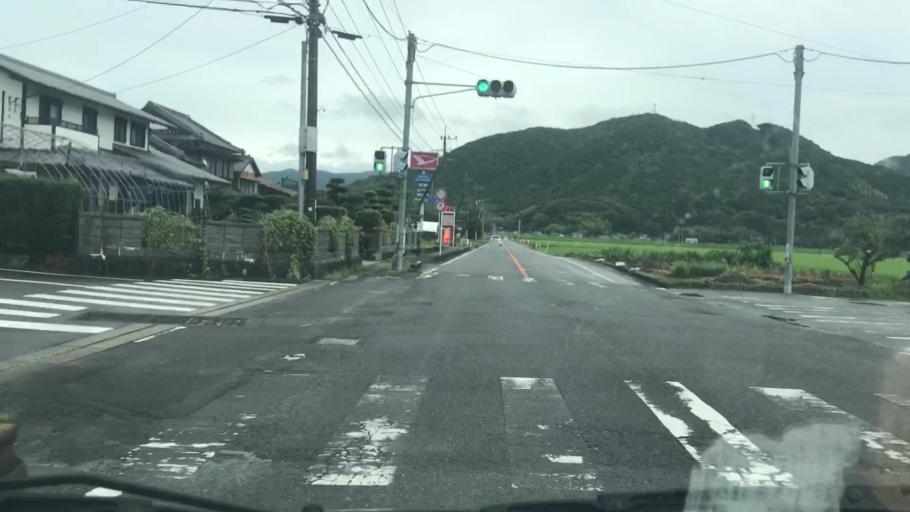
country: JP
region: Saga Prefecture
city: Takeocho-takeo
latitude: 33.1971
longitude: 130.0456
